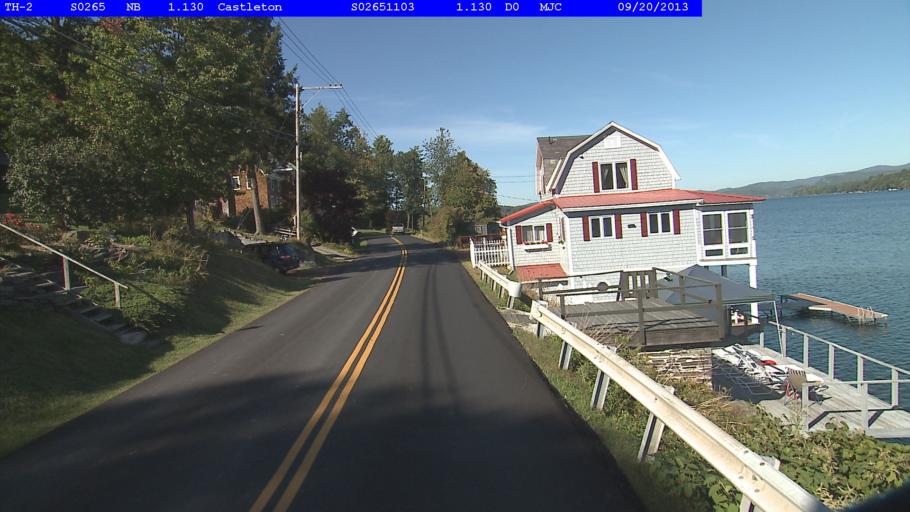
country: US
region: Vermont
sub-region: Rutland County
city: Fair Haven
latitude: 43.6202
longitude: -73.2301
